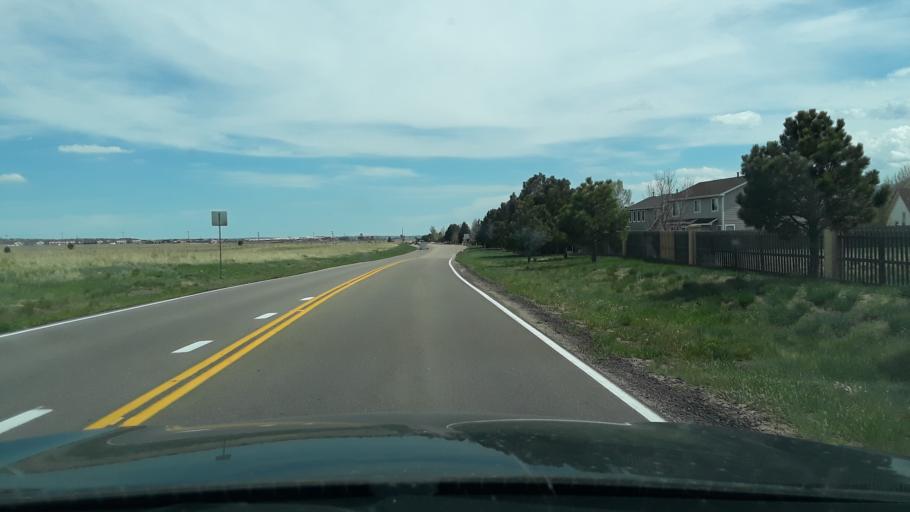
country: US
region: Colorado
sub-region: El Paso County
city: Monument
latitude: 39.0828
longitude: -104.8664
